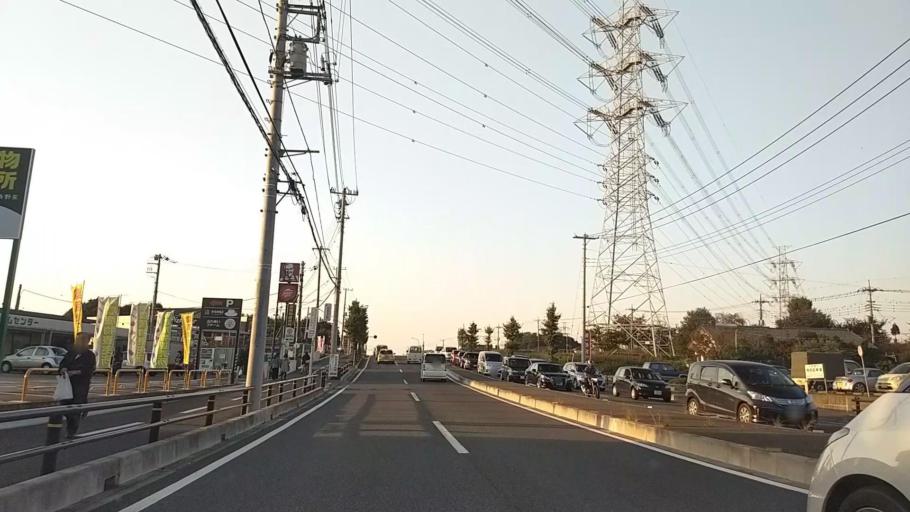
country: JP
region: Saitama
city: Sayama
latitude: 35.8603
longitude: 139.4300
